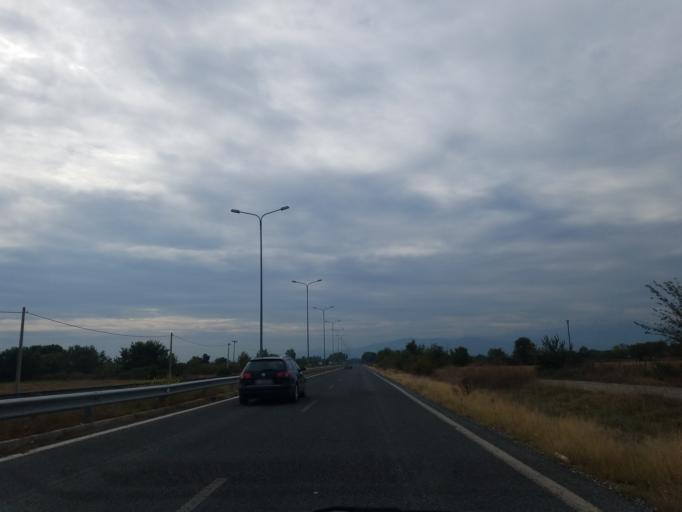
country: GR
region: Thessaly
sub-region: Trikala
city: Pyrgetos
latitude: 39.5541
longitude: 21.7340
